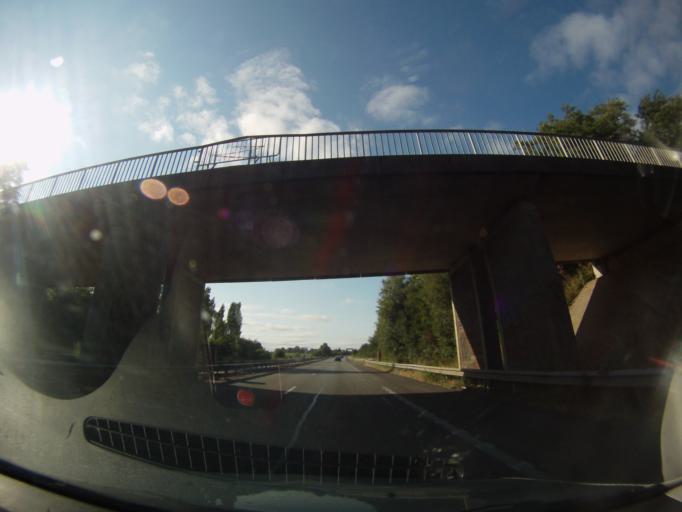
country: FR
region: Pays de la Loire
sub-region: Departement de la Loire-Atlantique
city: Treillieres
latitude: 47.3301
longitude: -1.6502
